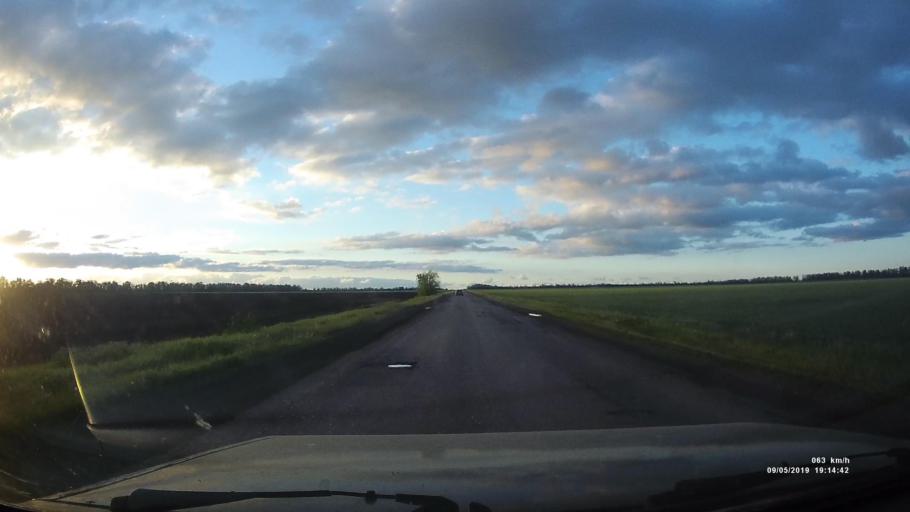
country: RU
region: Krasnodarskiy
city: Kanelovskaya
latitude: 46.7605
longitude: 39.2137
